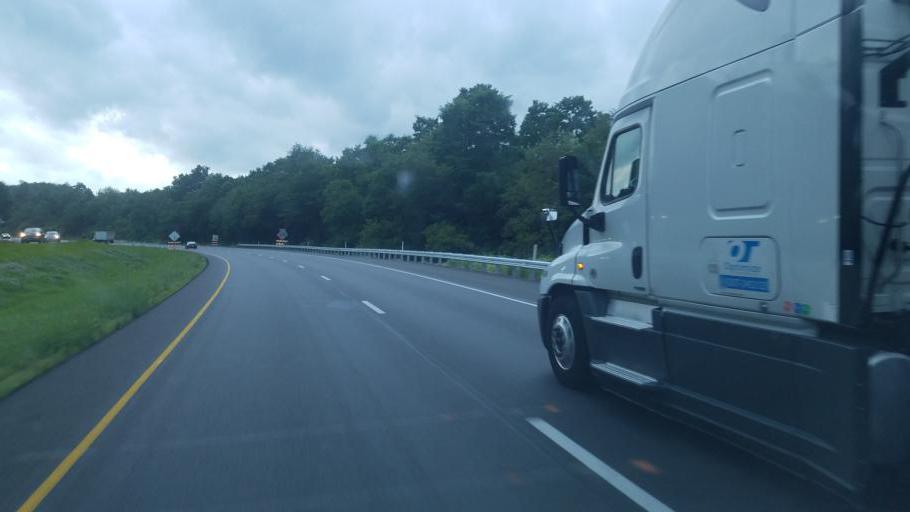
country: US
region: Pennsylvania
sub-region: Butler County
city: Zelienople
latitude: 40.7944
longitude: -80.1228
